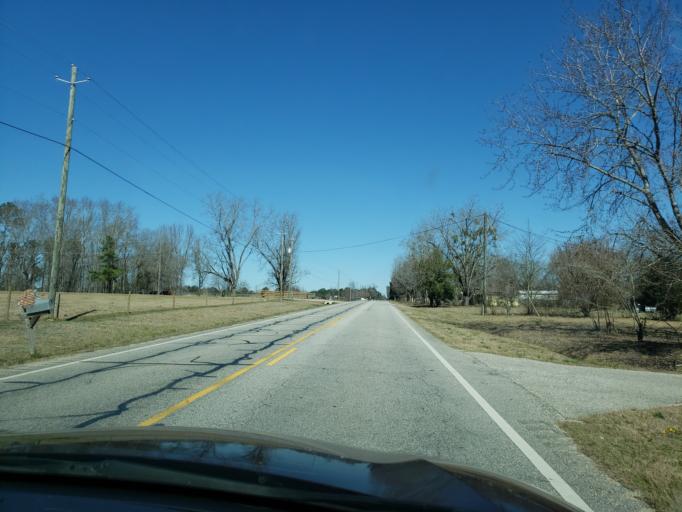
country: US
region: Alabama
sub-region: Macon County
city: Tuskegee
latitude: 32.5762
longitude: -85.6563
